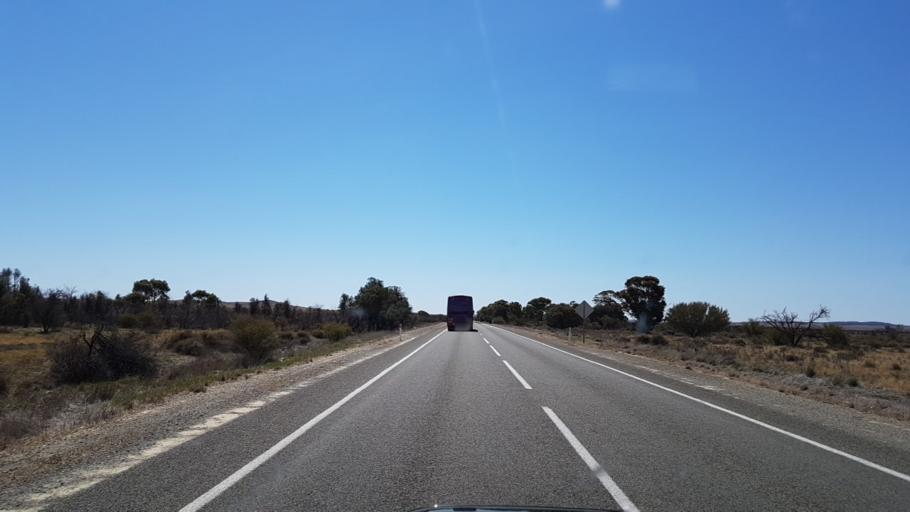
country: AU
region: South Australia
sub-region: Peterborough
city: Peterborough
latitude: -33.1829
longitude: 138.9058
